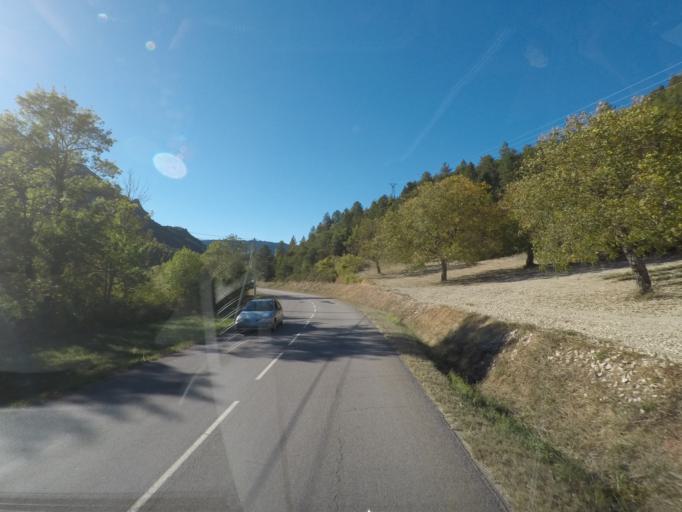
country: FR
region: Rhone-Alpes
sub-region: Departement de la Drome
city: Buis-les-Baronnies
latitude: 44.4747
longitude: 5.4115
